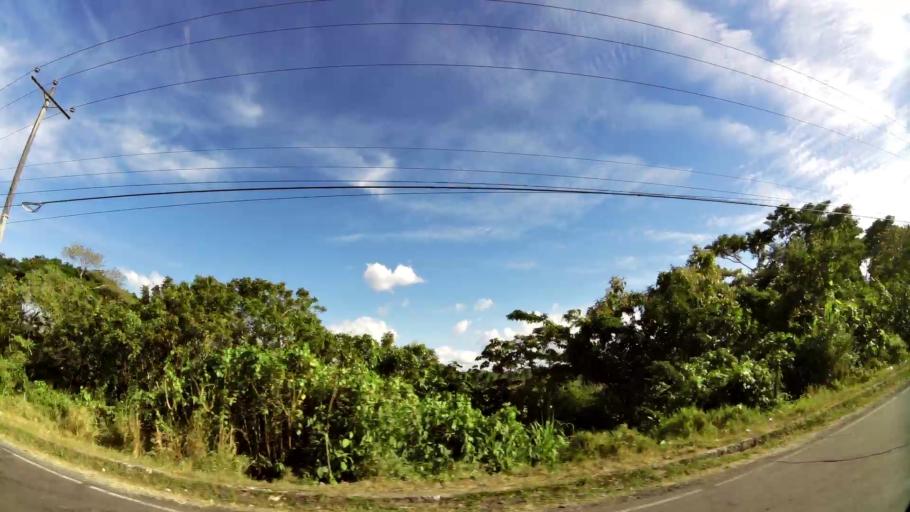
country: SV
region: Cuscatlan
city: Tecoluca
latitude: 13.7930
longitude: -89.0430
